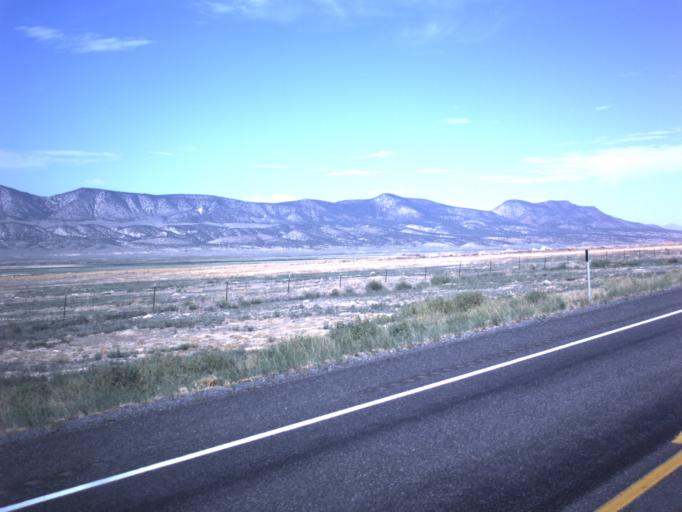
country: US
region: Utah
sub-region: Sanpete County
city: Gunnison
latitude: 39.2411
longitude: -111.8510
